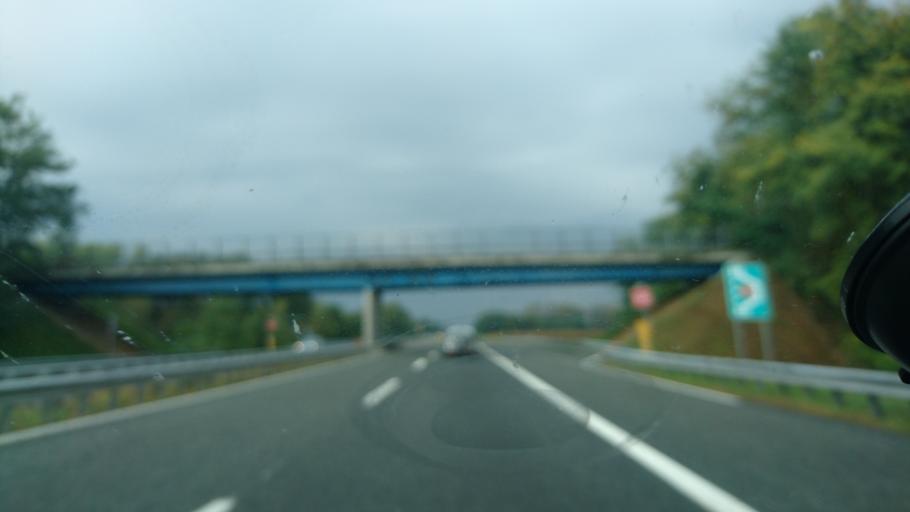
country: IT
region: Piedmont
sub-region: Provincia di Novara
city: Carpignano Sesia
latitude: 45.5512
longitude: 8.4224
